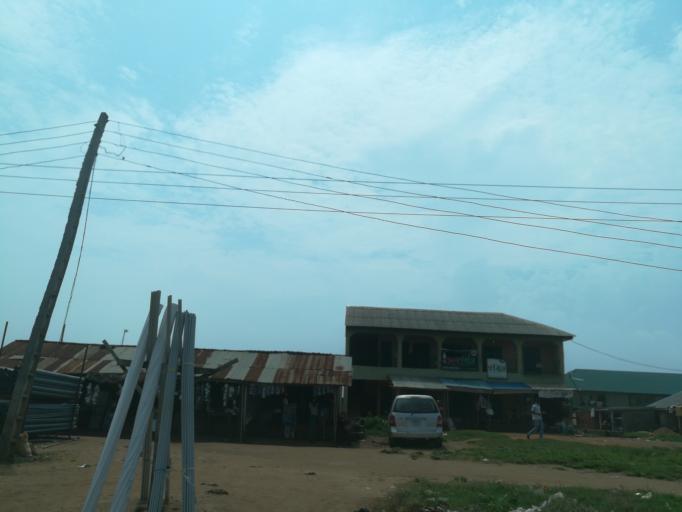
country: NG
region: Lagos
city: Ikorodu
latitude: 6.5906
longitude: 3.6245
